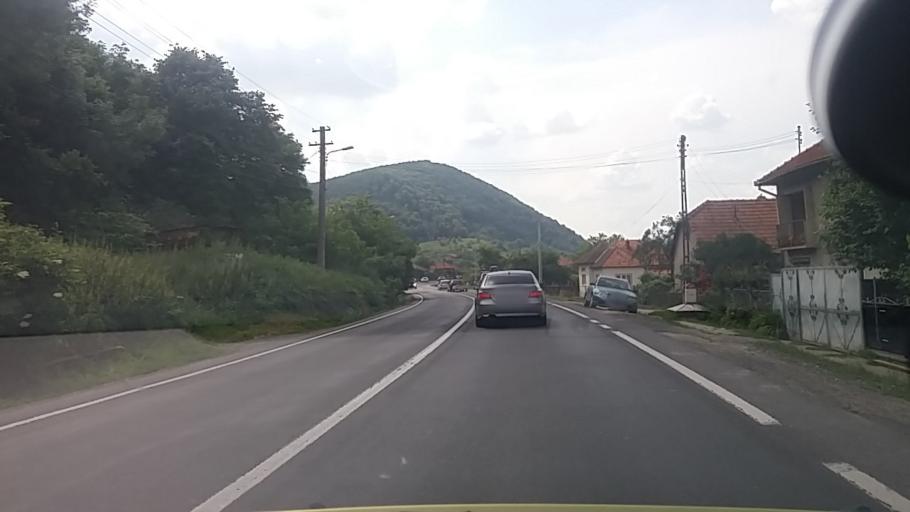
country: RO
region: Hunedoara
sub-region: Comuna Branisca
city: Branisca
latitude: 45.9157
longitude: 22.7348
